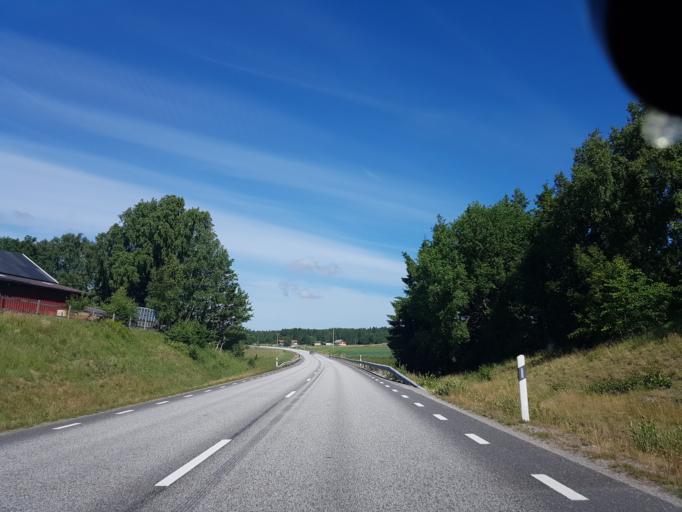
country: SE
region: Vaestra Goetaland
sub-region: Orust
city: Henan
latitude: 58.1397
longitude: 11.6458
